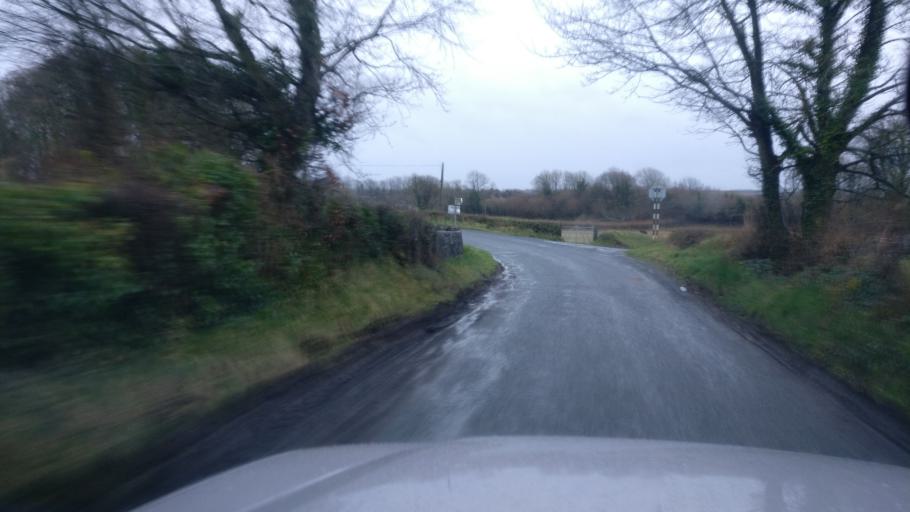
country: IE
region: Connaught
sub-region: County Galway
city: Ballinasloe
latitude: 53.2997
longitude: -8.2714
